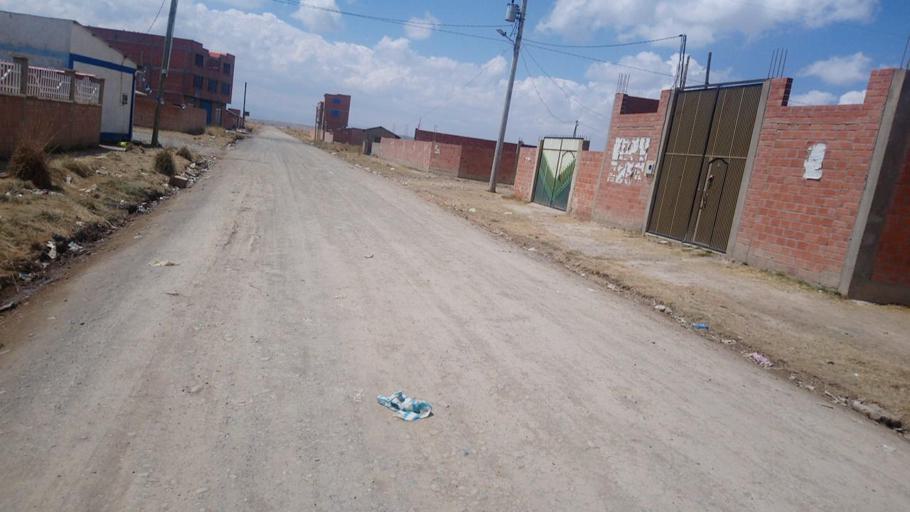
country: BO
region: La Paz
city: Batallas
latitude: -16.4083
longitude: -68.5399
